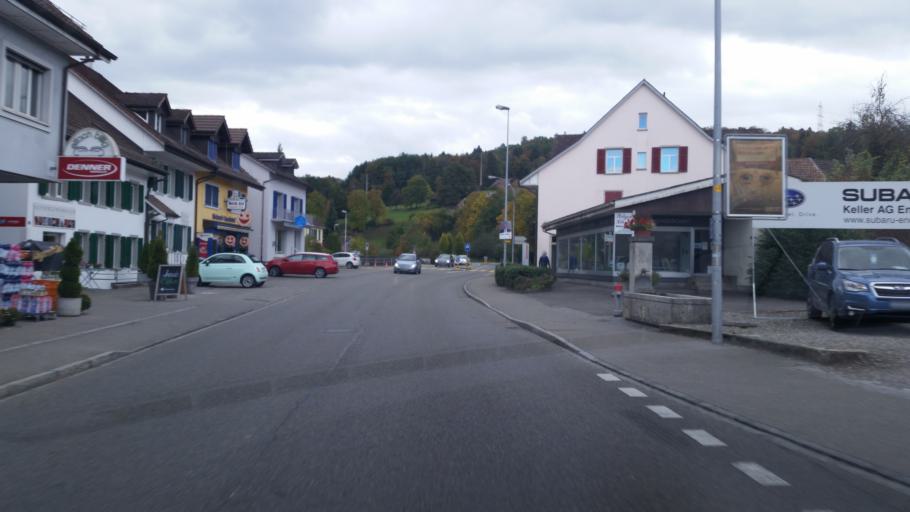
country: CH
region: Aargau
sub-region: Bezirk Zurzach
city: Oberendingen
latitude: 47.5374
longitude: 8.2905
